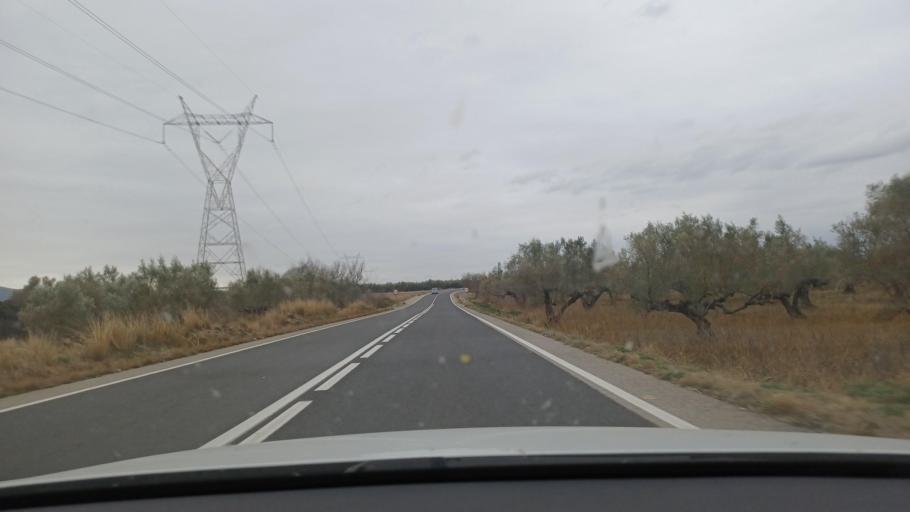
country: ES
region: Catalonia
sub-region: Provincia de Tarragona
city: Santa Barbara
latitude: 40.6757
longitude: 0.4489
